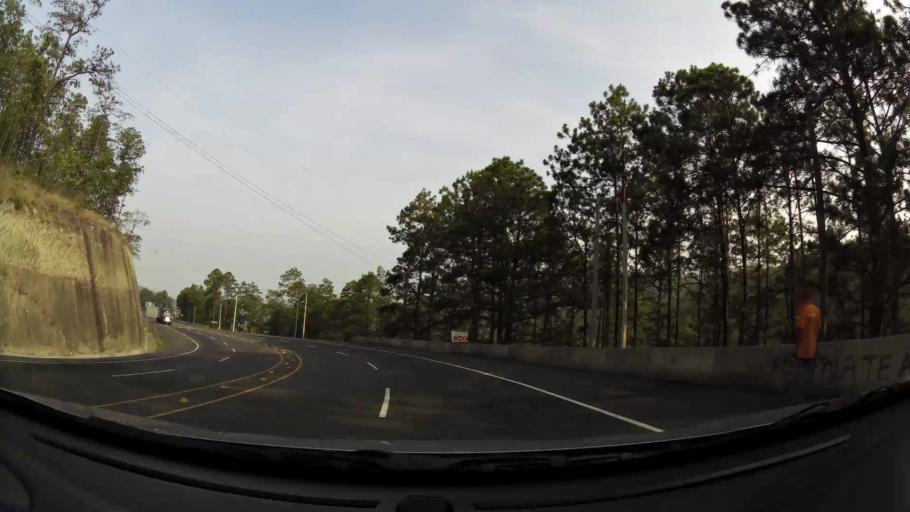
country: HN
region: Francisco Morazan
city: Zambrano
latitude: 14.2857
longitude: -87.4572
